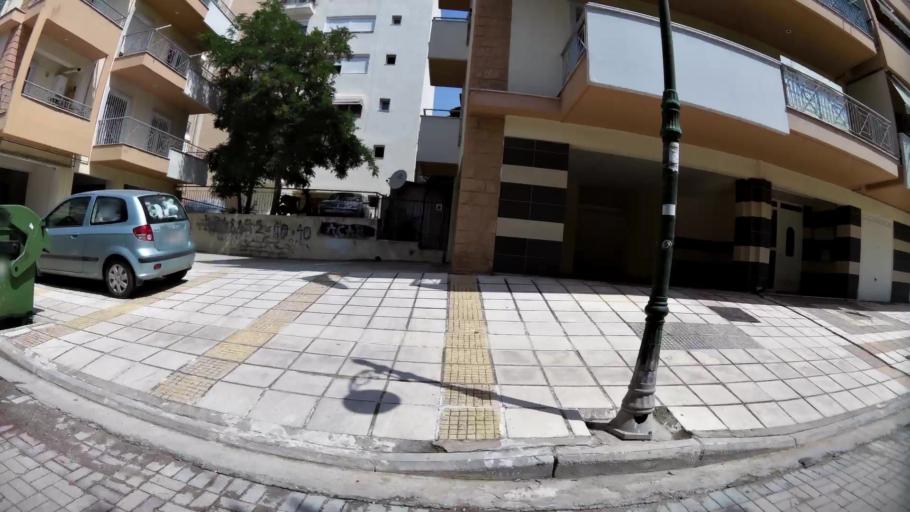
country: GR
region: Central Macedonia
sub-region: Nomos Thessalonikis
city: Evosmos
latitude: 40.6677
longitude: 22.9192
